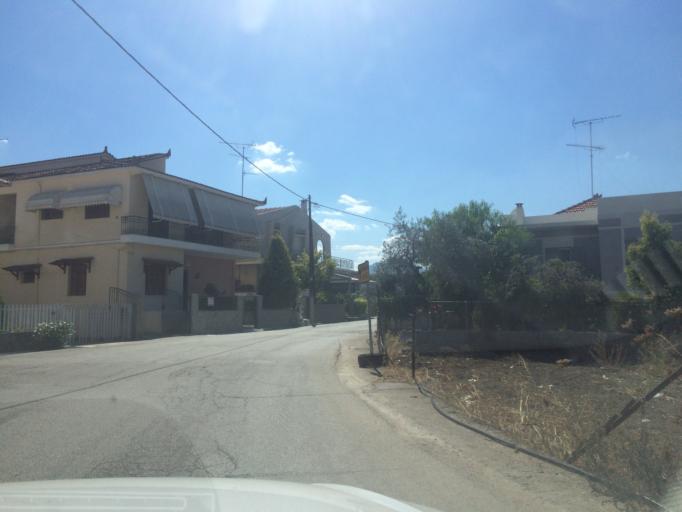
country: GR
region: Peloponnese
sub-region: Nomos Korinthias
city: Vokhaiko
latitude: 37.9481
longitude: 22.7933
